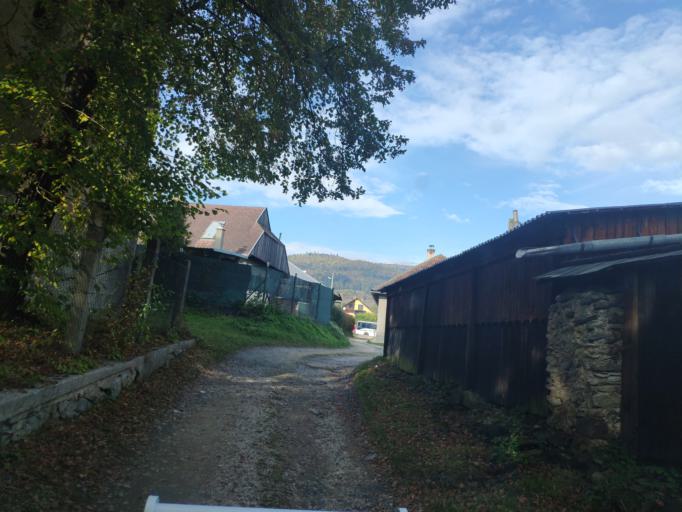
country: SK
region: Presovsky
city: Spisske Podhradie
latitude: 48.8150
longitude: 20.7125
